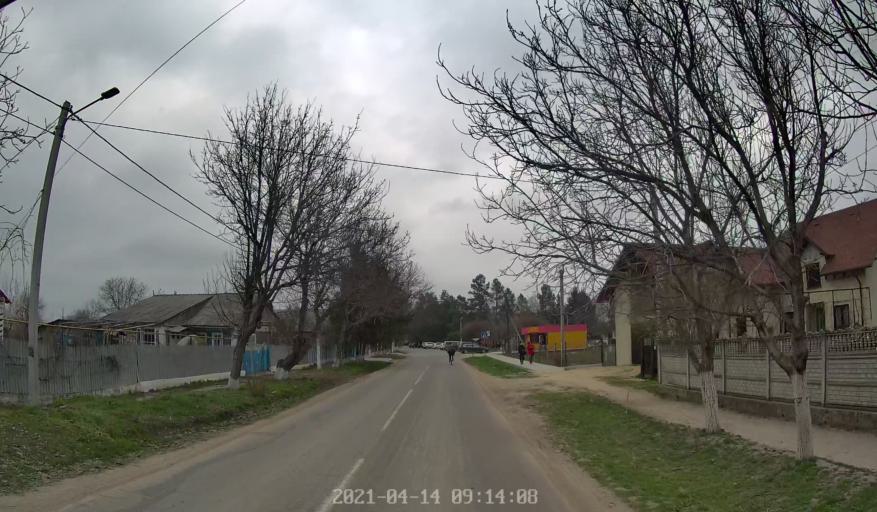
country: MD
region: Chisinau
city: Vadul lui Voda
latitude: 47.1065
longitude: 29.1142
